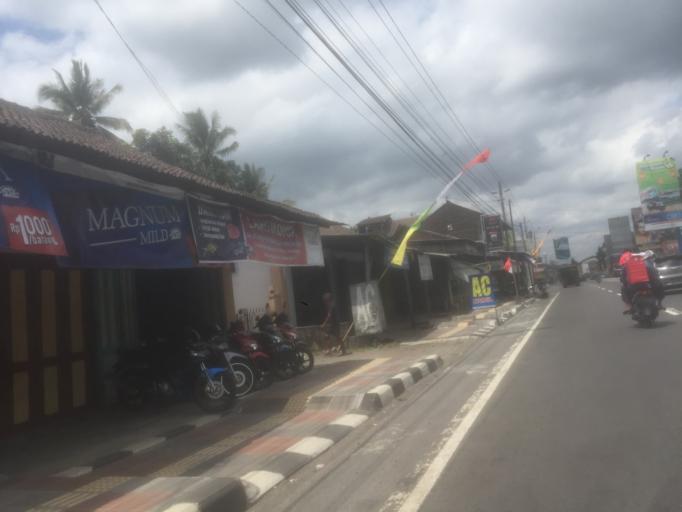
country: ID
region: Central Java
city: Muntilan
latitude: -7.6391
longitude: 110.3218
